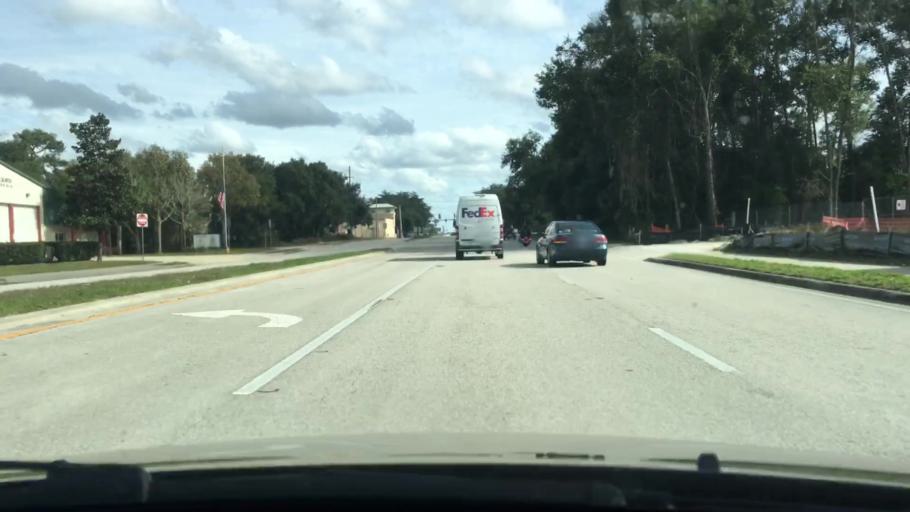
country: US
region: Florida
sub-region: Volusia County
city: North DeLand
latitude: 29.0546
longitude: -81.3082
